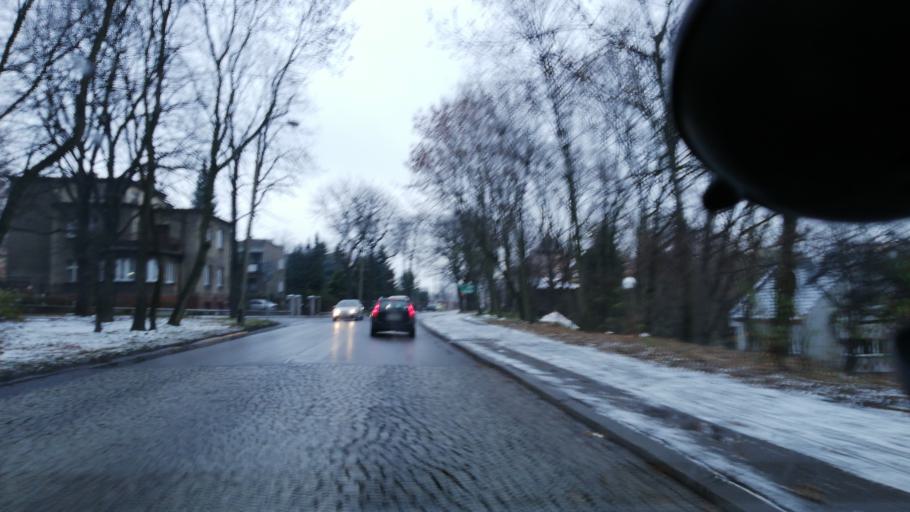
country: PL
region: Silesian Voivodeship
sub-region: Chorzow
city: Chorzow
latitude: 50.2953
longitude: 18.9678
